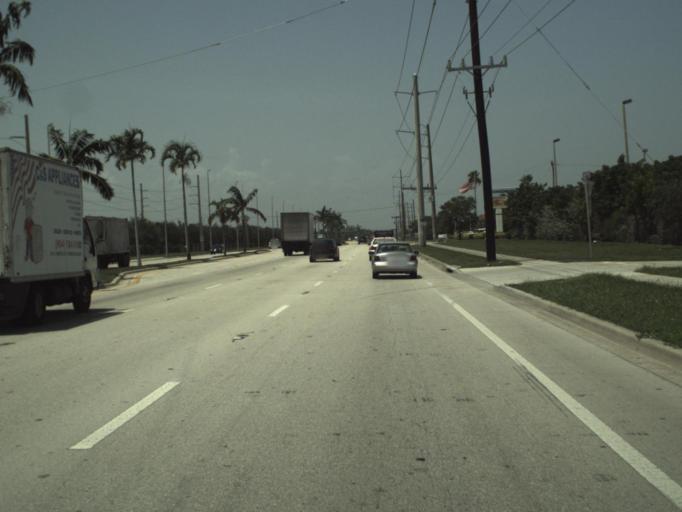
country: US
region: Florida
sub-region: Broward County
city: Tedder
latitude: 26.2832
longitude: -80.1522
